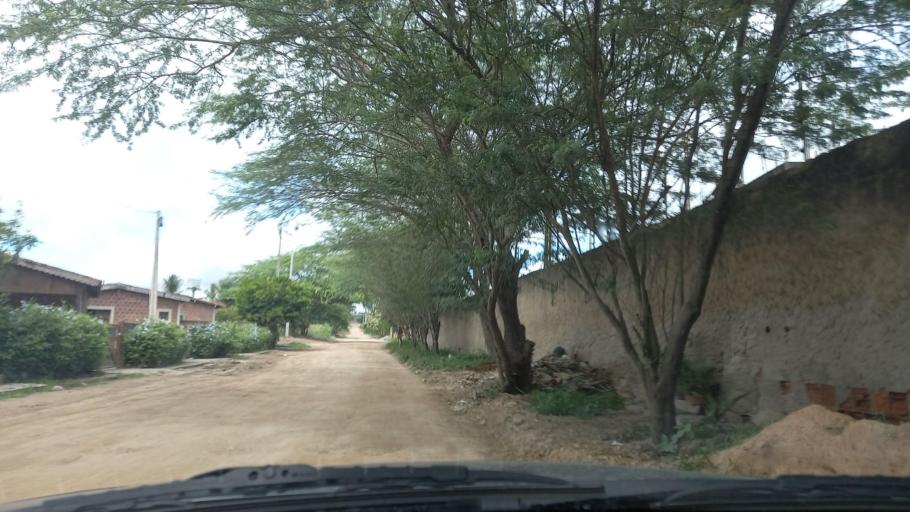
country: BR
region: Pernambuco
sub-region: Gravata
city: Gravata
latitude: -8.1944
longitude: -35.5855
